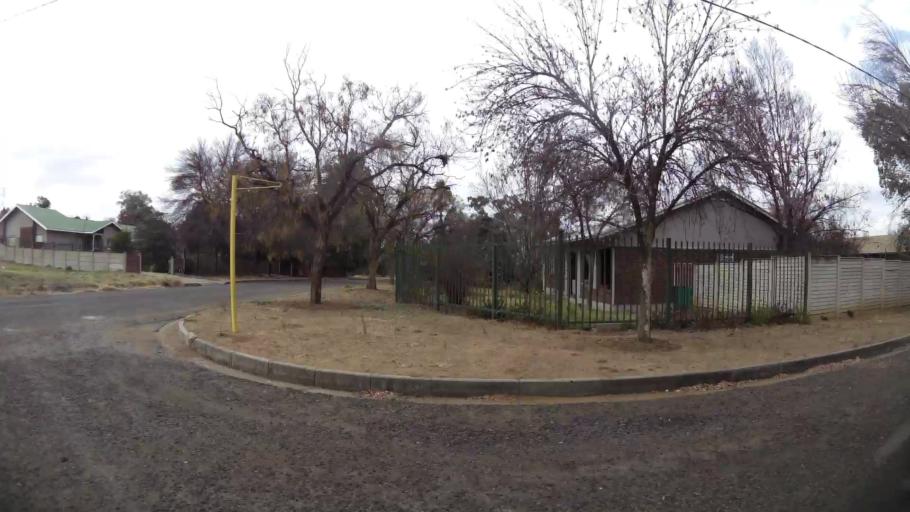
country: ZA
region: Orange Free State
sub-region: Fezile Dabi District Municipality
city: Kroonstad
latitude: -27.6492
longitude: 27.2407
